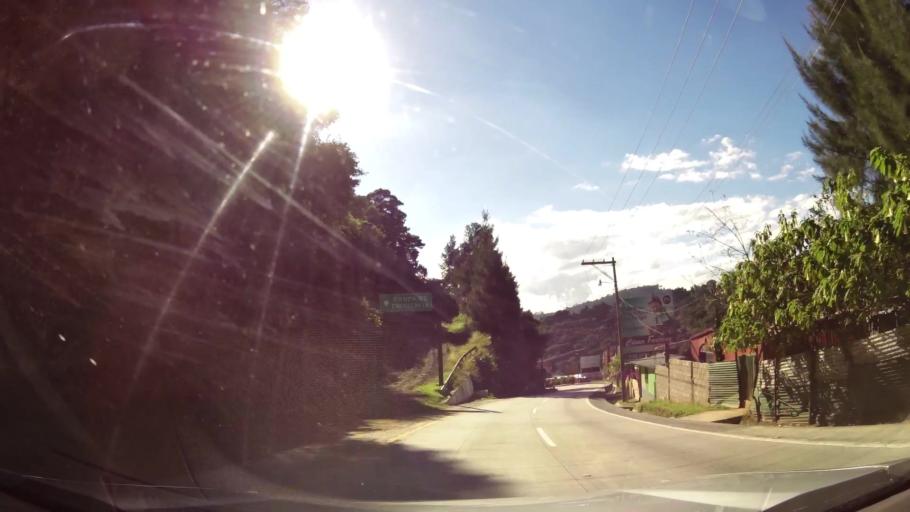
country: GT
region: Sacatepequez
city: Santa Lucia Milpas Altas
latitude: 14.5761
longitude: -90.6830
